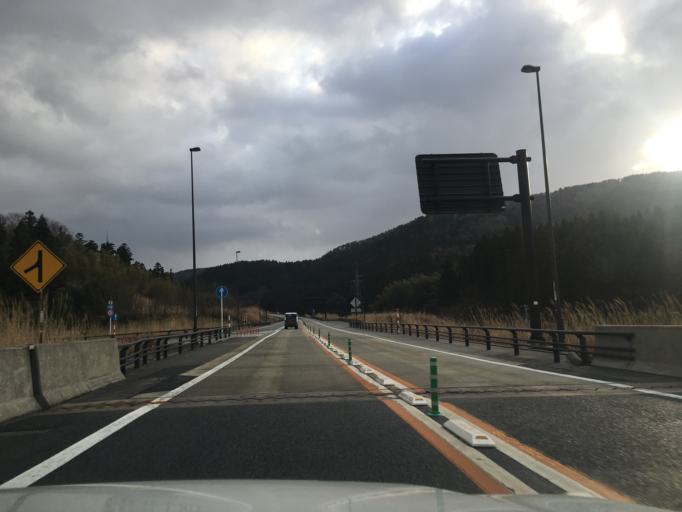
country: JP
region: Yamagata
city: Tsuruoka
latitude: 38.6894
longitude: 139.6733
